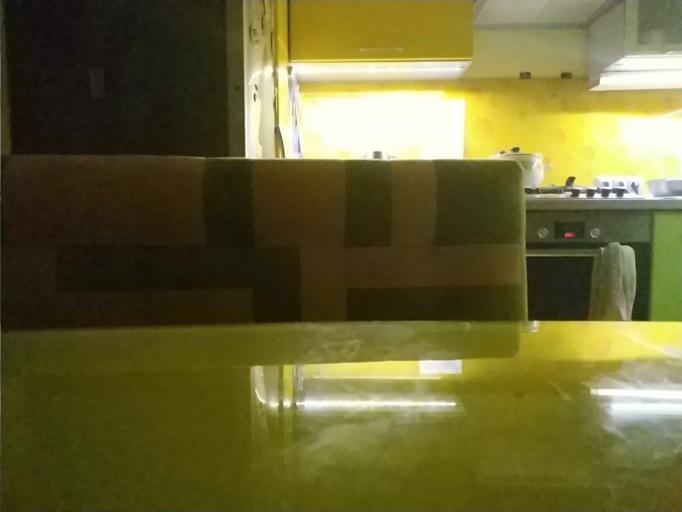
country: RU
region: Republic of Karelia
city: Pyaozerskiy
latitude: 65.9565
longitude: 30.4015
